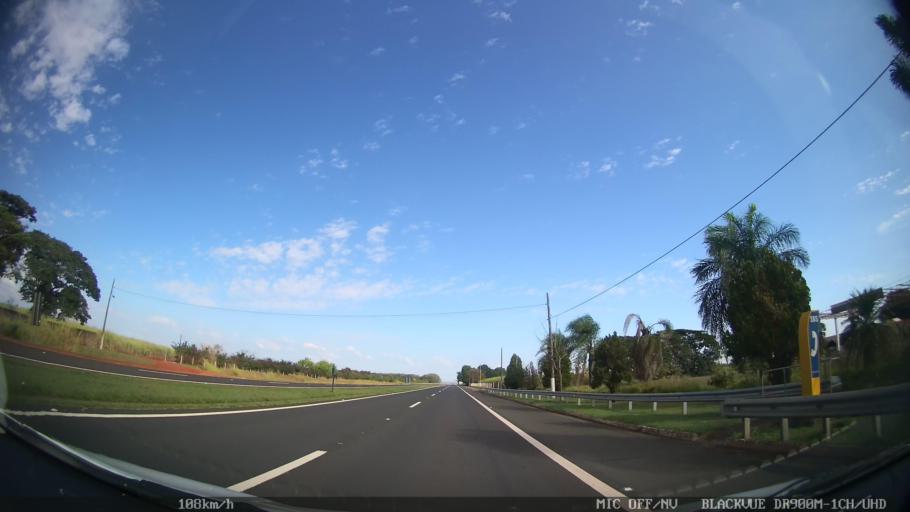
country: BR
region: Sao Paulo
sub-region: Iracemapolis
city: Iracemapolis
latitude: -22.6422
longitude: -47.5103
